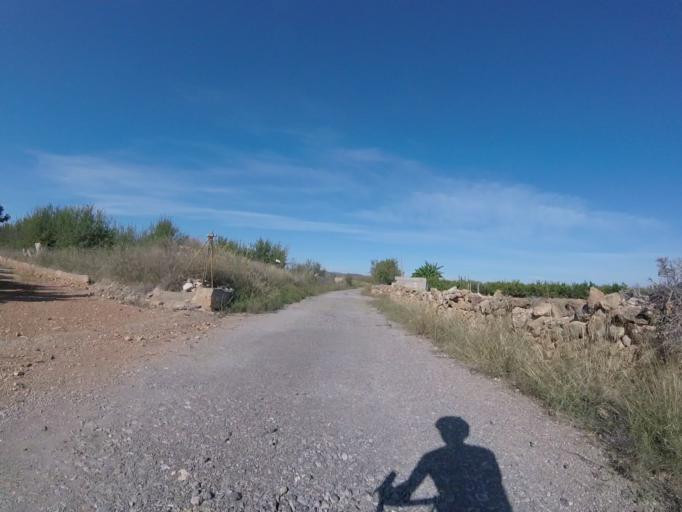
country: ES
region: Valencia
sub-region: Provincia de Castello
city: Torreblanca
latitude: 40.2094
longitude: 0.2338
